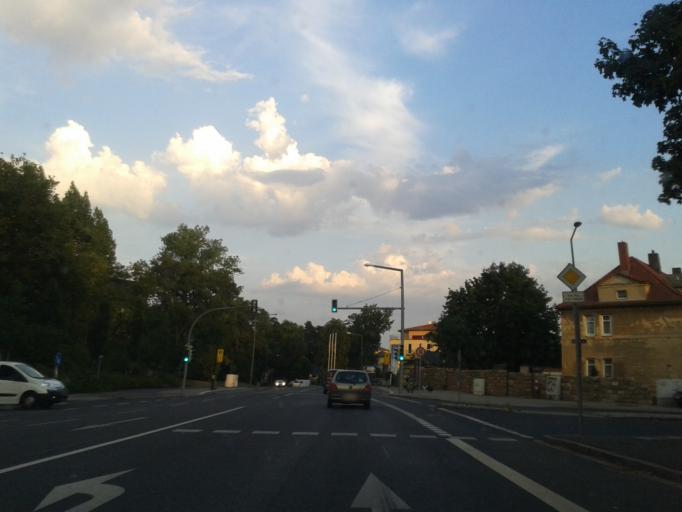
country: DE
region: Saxony
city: Dresden
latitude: 51.0996
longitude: 13.7152
